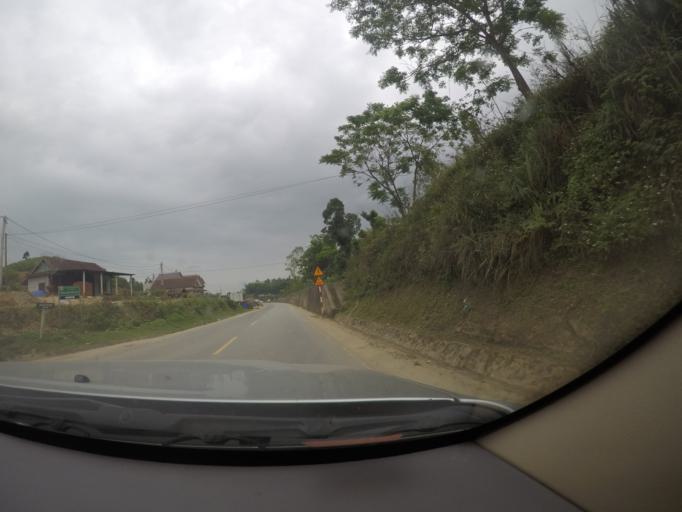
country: VN
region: Quang Binh
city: Ba Don
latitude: 17.6159
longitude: 106.3710
